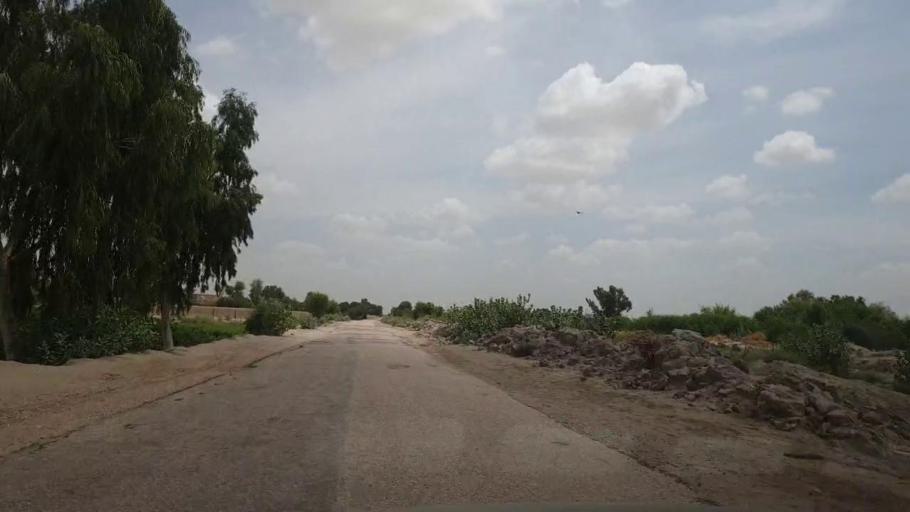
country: PK
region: Sindh
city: Kot Diji
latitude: 27.2107
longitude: 69.1147
